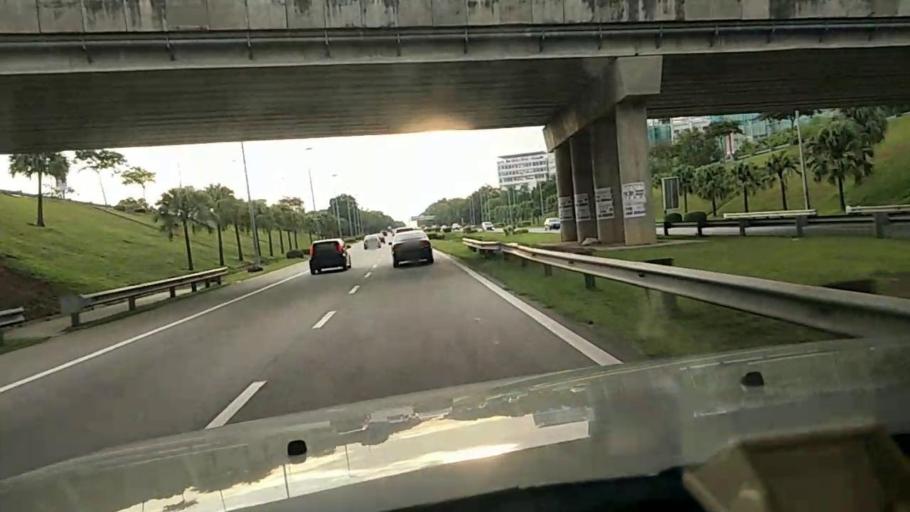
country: MY
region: Selangor
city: Klang
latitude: 3.1075
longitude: 101.4563
